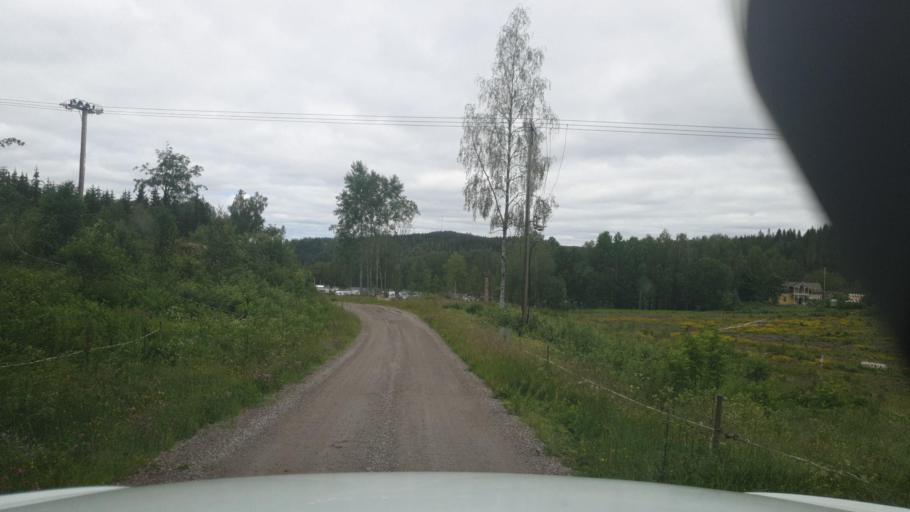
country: NO
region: Ostfold
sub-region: Romskog
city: Romskog
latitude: 59.8185
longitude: 11.9956
